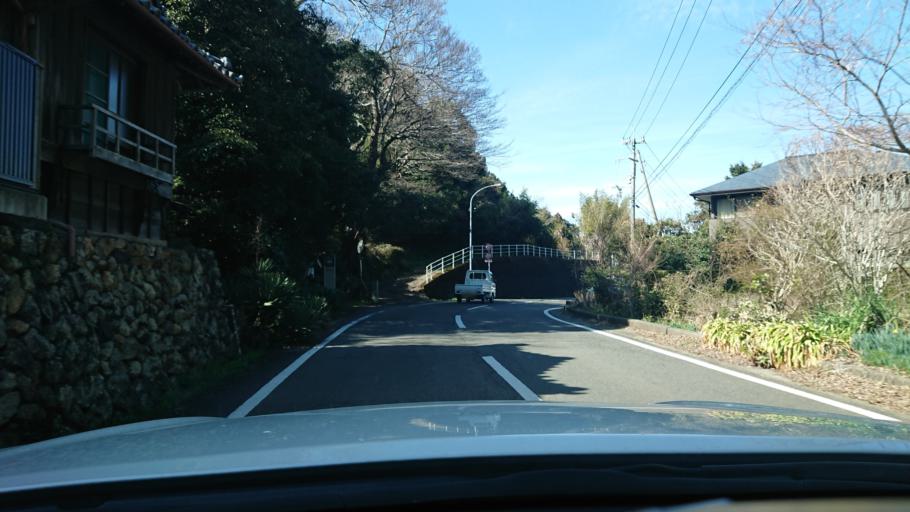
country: JP
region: Tokushima
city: Komatsushimacho
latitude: 33.9710
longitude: 134.5931
